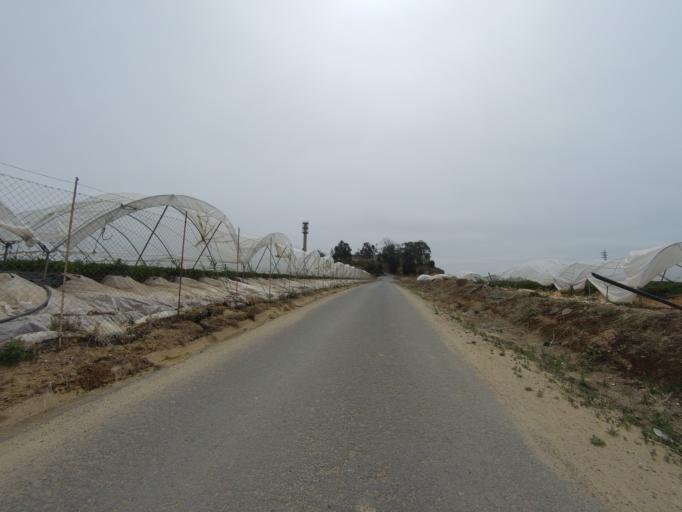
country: ES
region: Andalusia
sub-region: Provincia de Huelva
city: Palos de la Frontera
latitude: 37.2421
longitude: -6.8845
